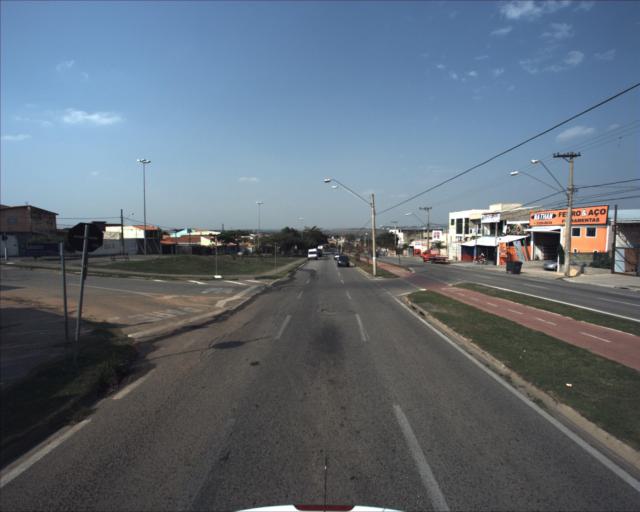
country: BR
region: Sao Paulo
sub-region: Sorocaba
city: Sorocaba
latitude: -23.4351
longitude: -47.4665
